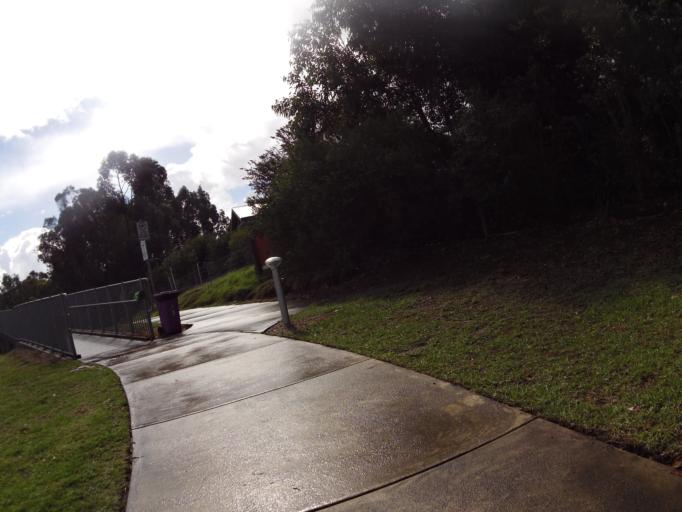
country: AU
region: Western Australia
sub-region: Donnybrook-Balingup
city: Donnybrook
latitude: -33.5746
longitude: 115.8264
